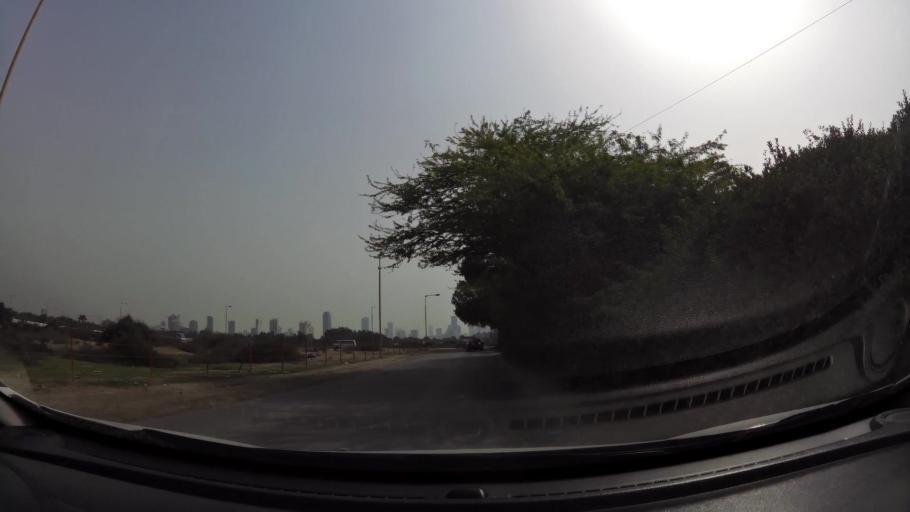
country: BH
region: Manama
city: Jidd Hafs
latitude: 26.2266
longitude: 50.5214
